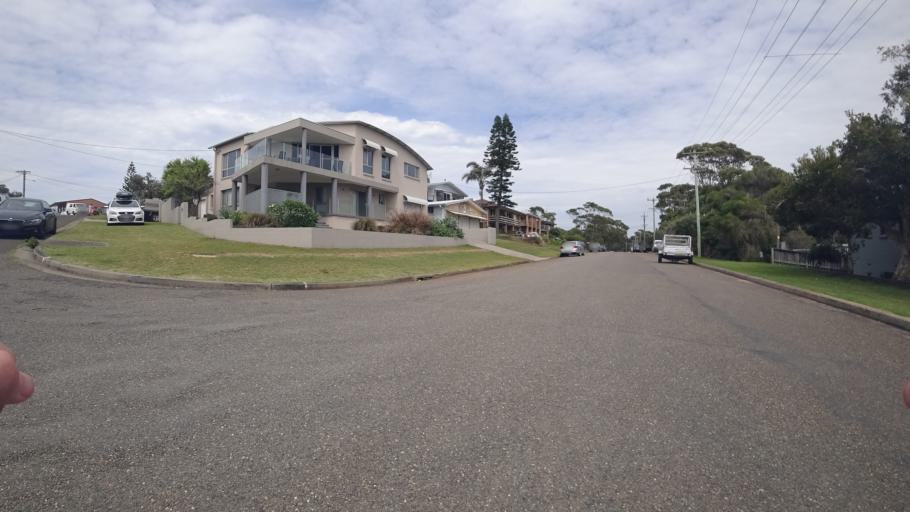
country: AU
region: New South Wales
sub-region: Shoalhaven Shire
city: Milton
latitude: -35.2561
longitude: 150.5254
